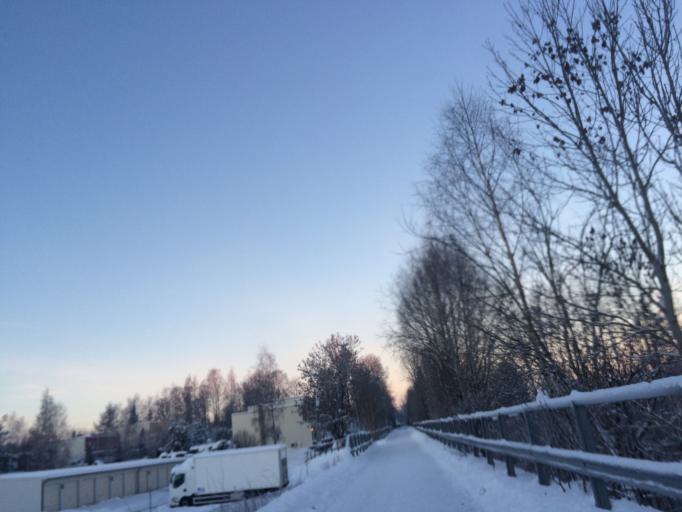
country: NO
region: Akershus
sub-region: Ski
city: Ski
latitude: 59.7087
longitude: 10.8347
